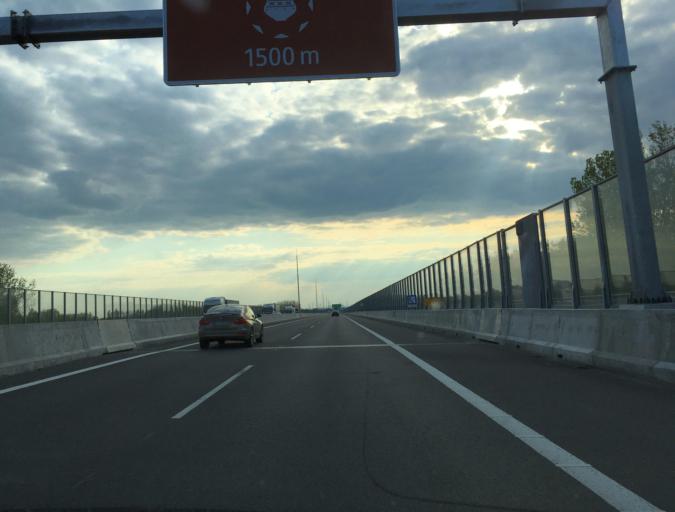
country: SK
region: Bratislavsky
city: Bratislava
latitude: 48.0828
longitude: 17.1493
